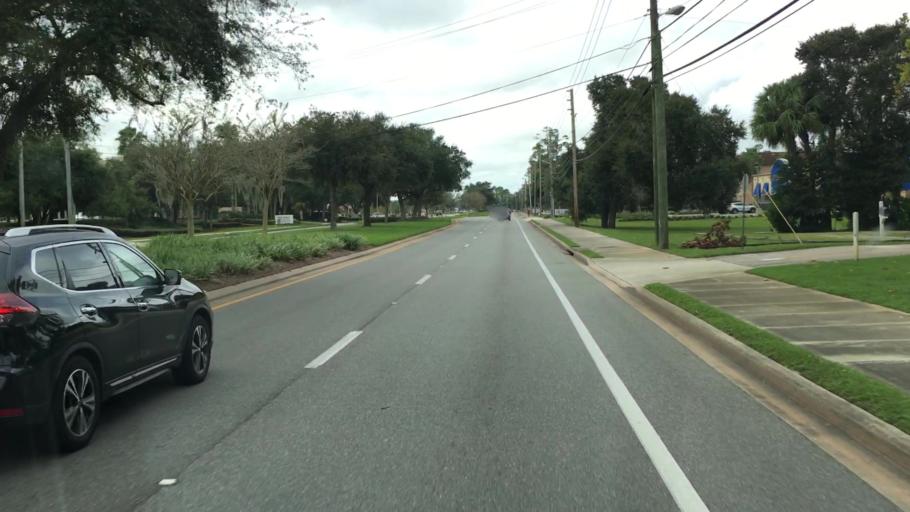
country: US
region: Florida
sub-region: Volusia County
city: Ormond Beach
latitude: 29.2666
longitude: -81.1032
